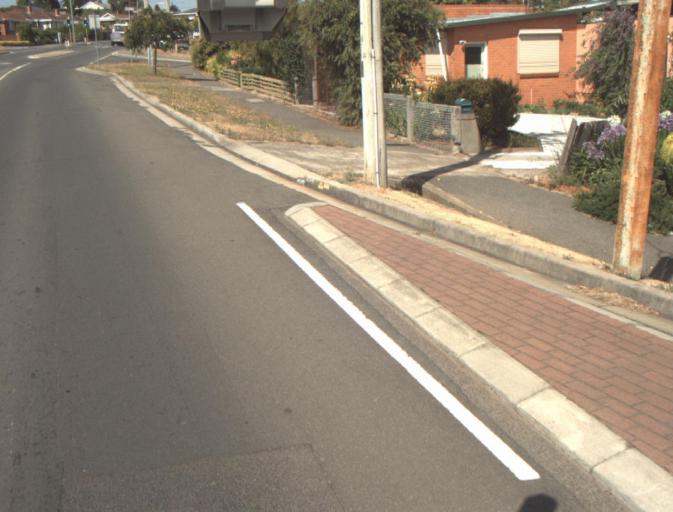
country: AU
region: Tasmania
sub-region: Launceston
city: Summerhill
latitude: -41.4716
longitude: 147.1316
